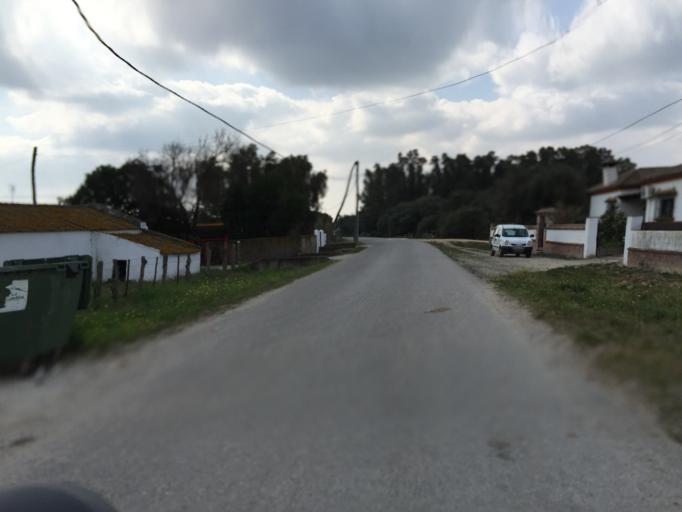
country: ES
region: Andalusia
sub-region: Provincia de Cadiz
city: Benalup-Casas Viejas
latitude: 36.3206
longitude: -5.8844
